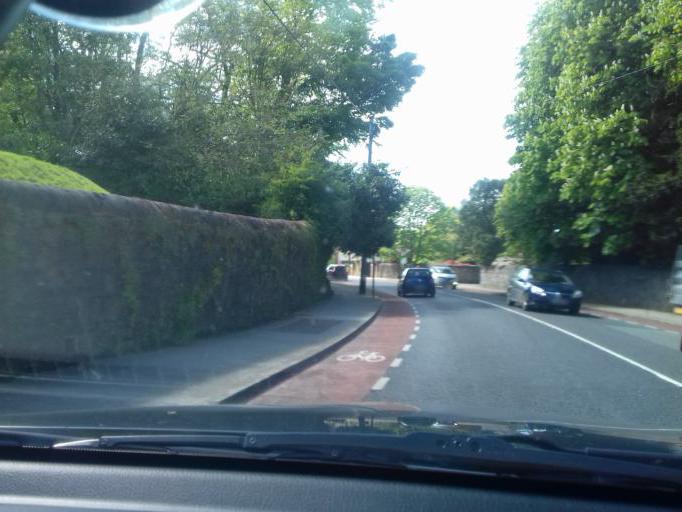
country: IE
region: Munster
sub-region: Waterford
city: Waterford
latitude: 52.2498
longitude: -7.0924
